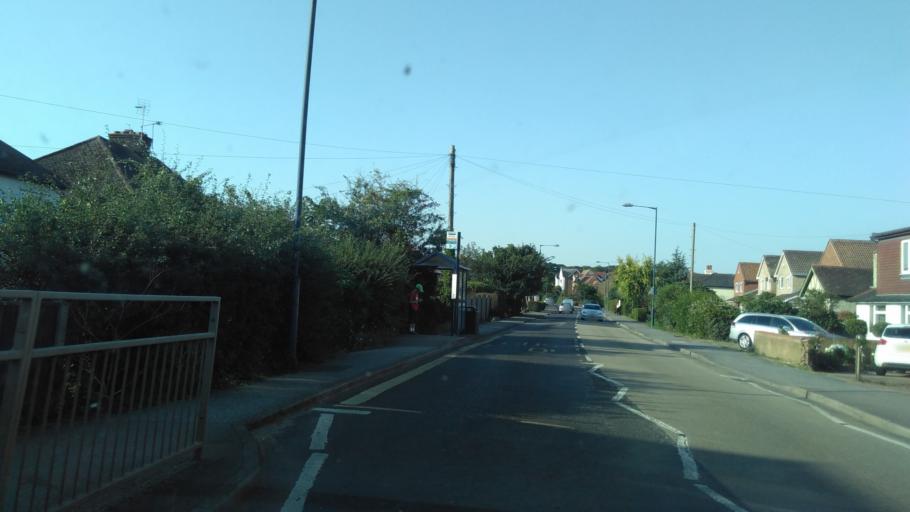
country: GB
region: England
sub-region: Kent
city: Whitstable
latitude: 51.3445
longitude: 1.0217
